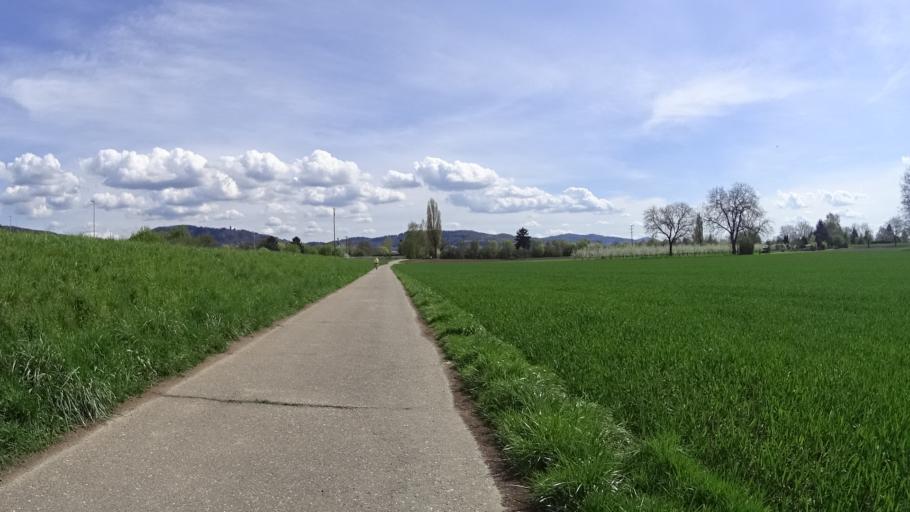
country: DE
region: Baden-Wuerttemberg
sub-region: Karlsruhe Region
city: Hemsbach
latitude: 49.5664
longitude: 8.6471
